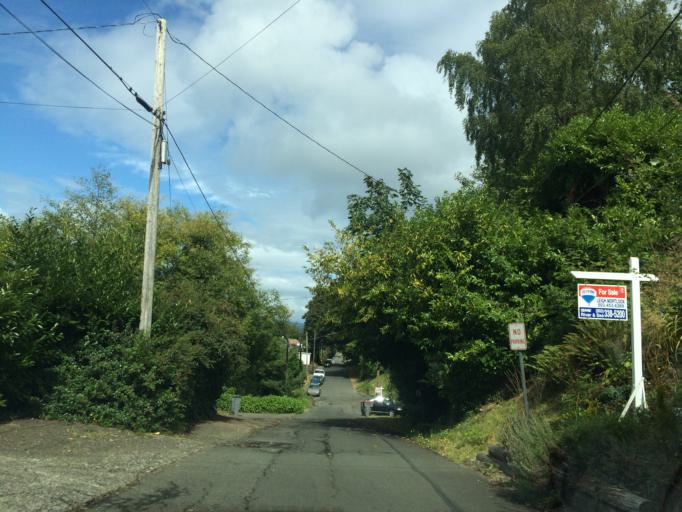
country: US
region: Oregon
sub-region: Clatsop County
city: Astoria
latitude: 46.1876
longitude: -123.8144
